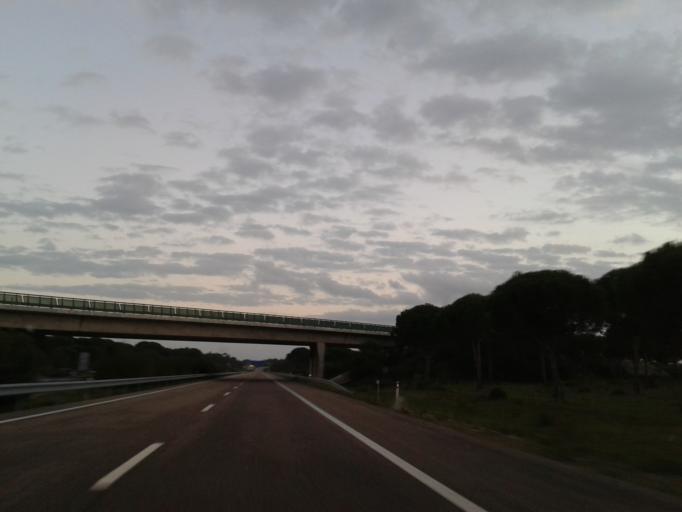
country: PT
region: Evora
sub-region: Vendas Novas
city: Vendas Novas
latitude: 38.6213
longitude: -8.6551
